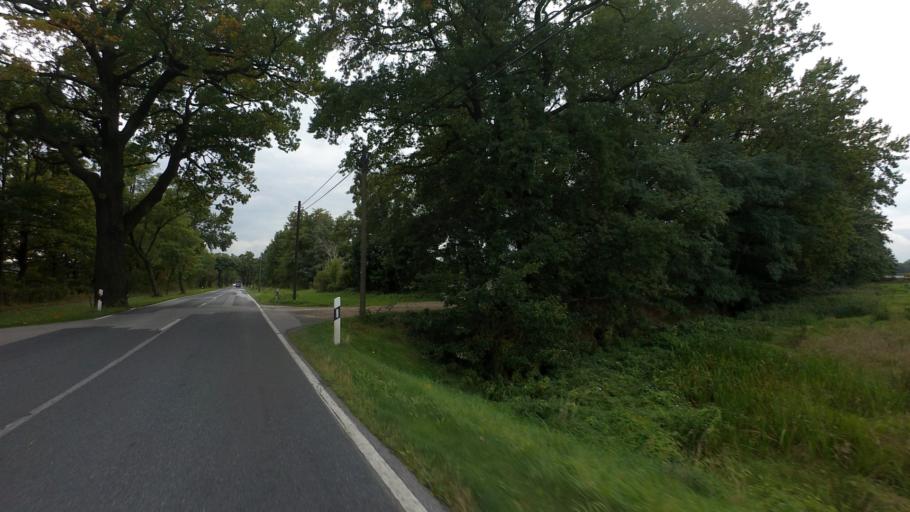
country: DE
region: Saxony
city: Konigswartha
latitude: 51.3244
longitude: 14.3387
